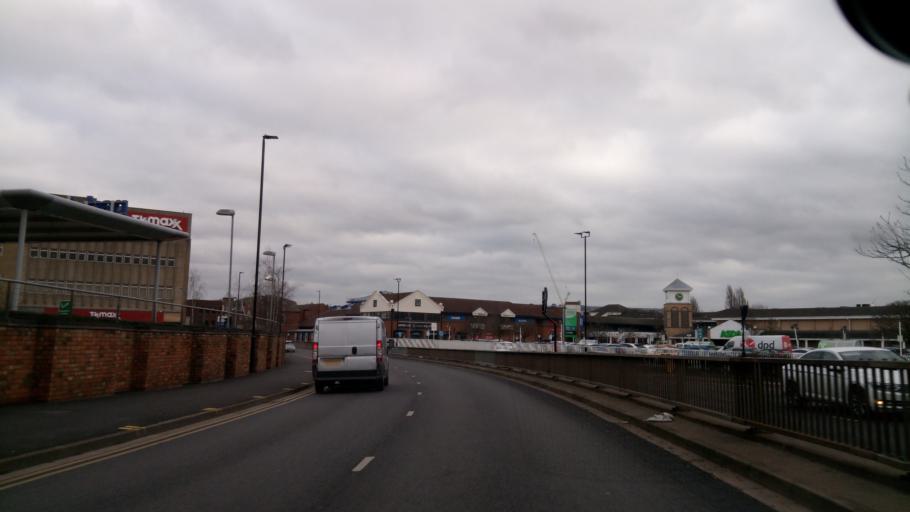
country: GB
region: England
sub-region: Peterborough
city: Peterborough
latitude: 52.5706
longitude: -0.2454
